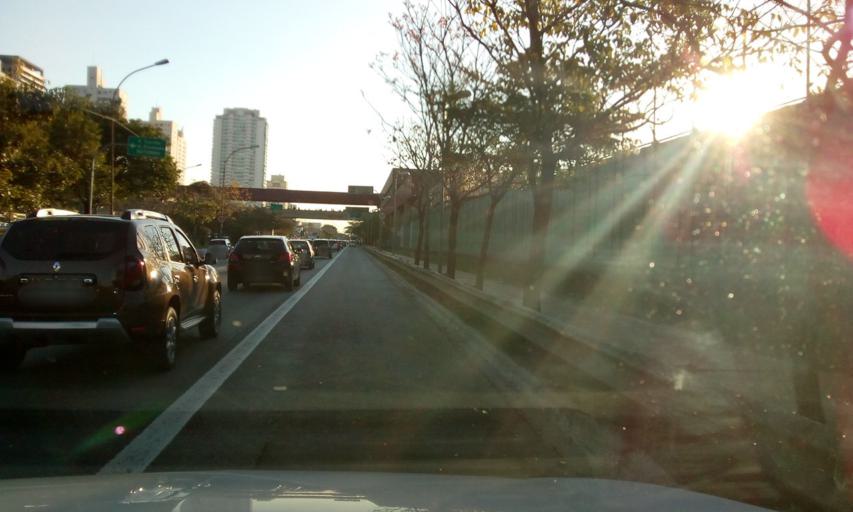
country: BR
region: Sao Paulo
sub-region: Sao Paulo
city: Sao Paulo
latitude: -23.5377
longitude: -46.5626
